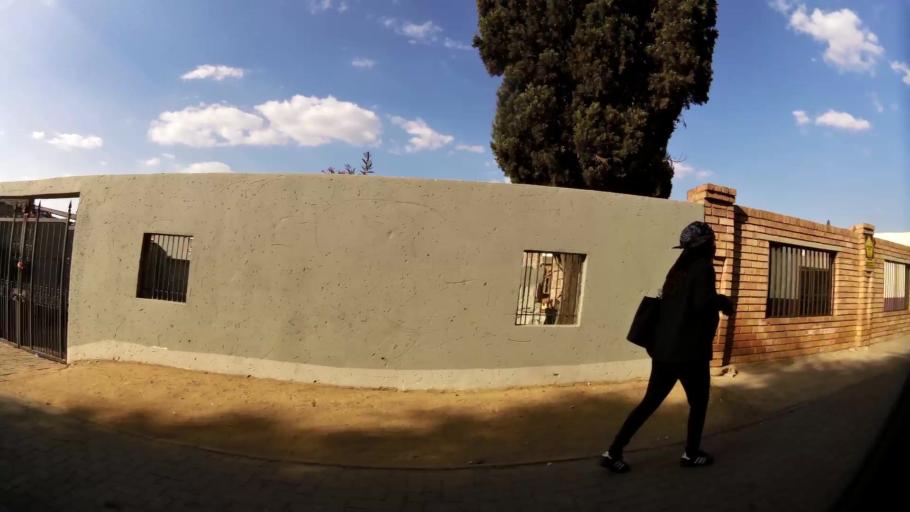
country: ZA
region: Gauteng
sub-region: City of Johannesburg Metropolitan Municipality
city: Soweto
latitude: -26.2241
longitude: 27.8729
